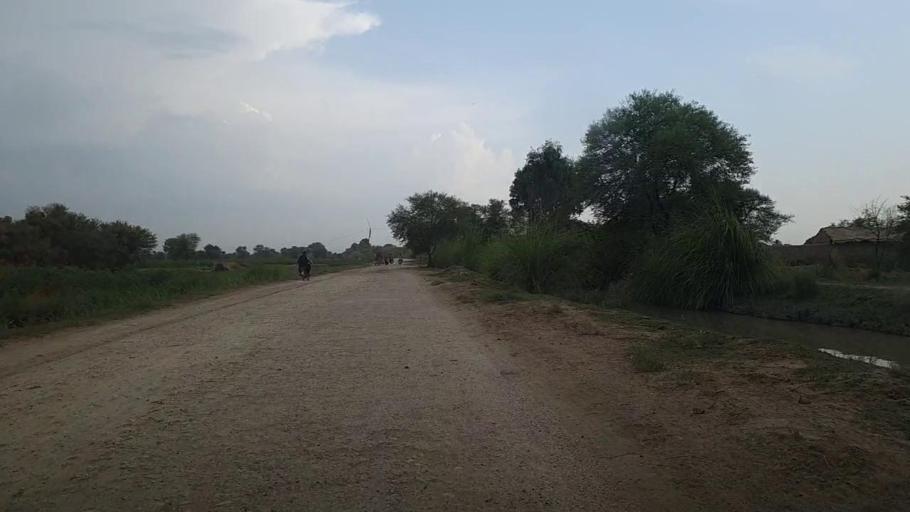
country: PK
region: Sindh
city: Khanpur
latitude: 27.8428
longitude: 69.4848
